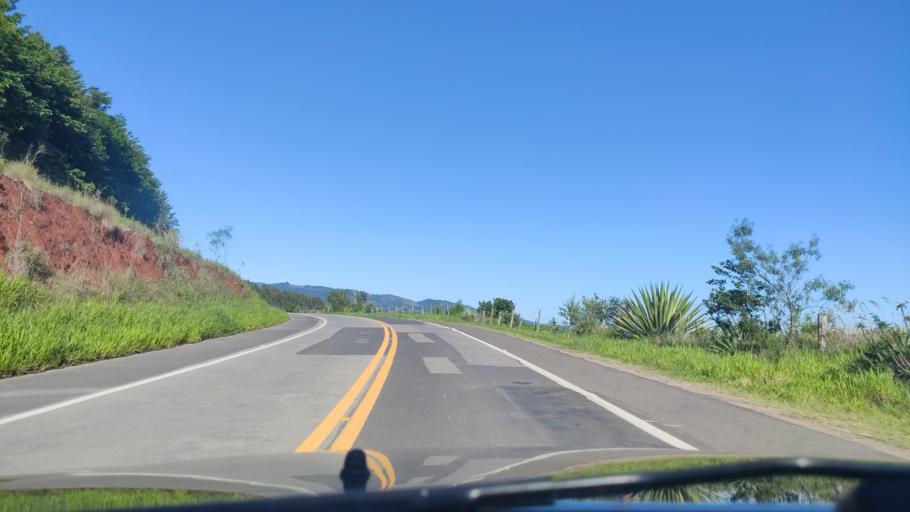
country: BR
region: Sao Paulo
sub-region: Socorro
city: Socorro
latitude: -22.5585
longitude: -46.5984
